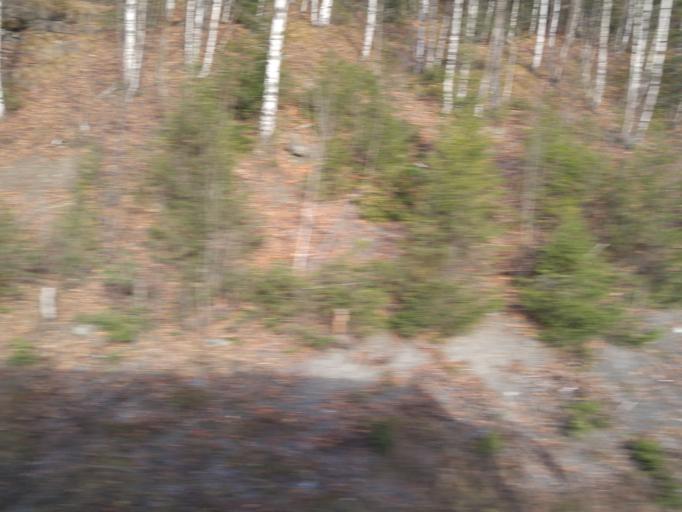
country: NO
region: Oppland
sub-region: Nord-Aurdal
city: Fagernes
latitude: 61.0523
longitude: 9.1730
